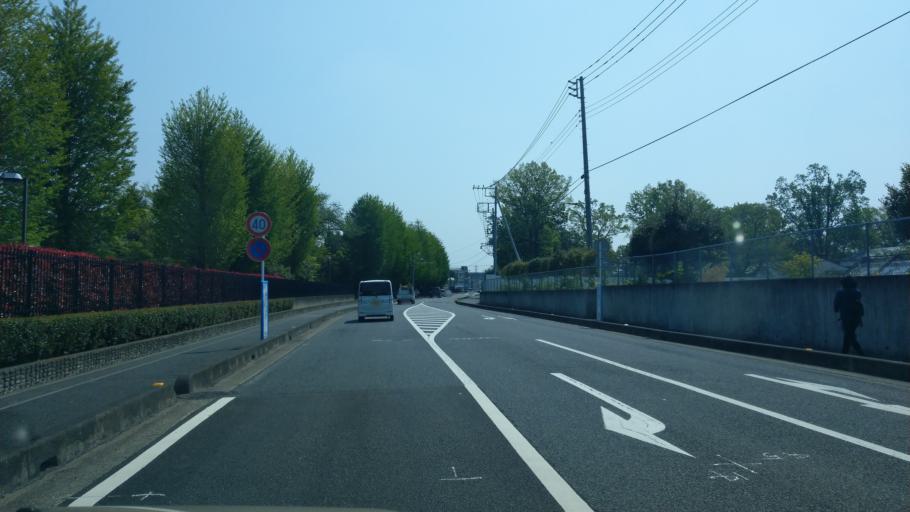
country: JP
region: Saitama
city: Yono
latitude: 35.9188
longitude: 139.6019
